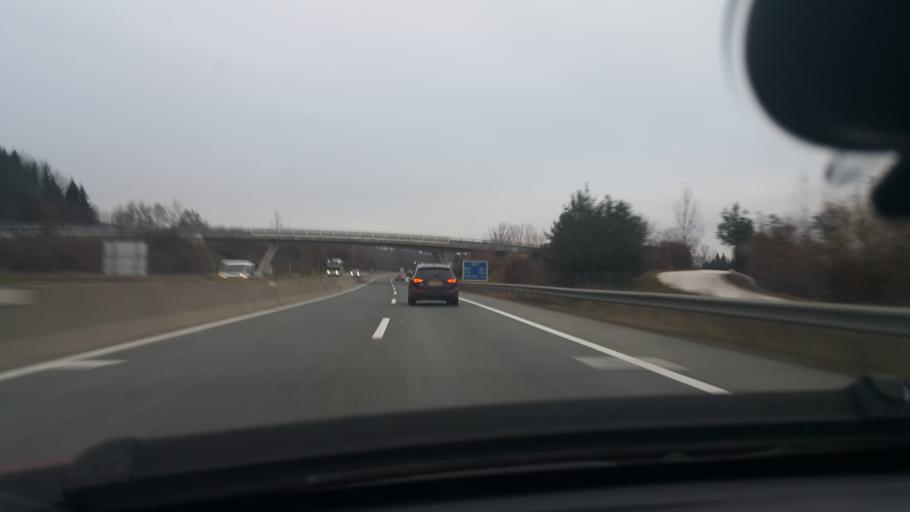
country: AT
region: Carinthia
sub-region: Politischer Bezirk Klagenfurt Land
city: Ebenthal
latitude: 46.6439
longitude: 14.3764
